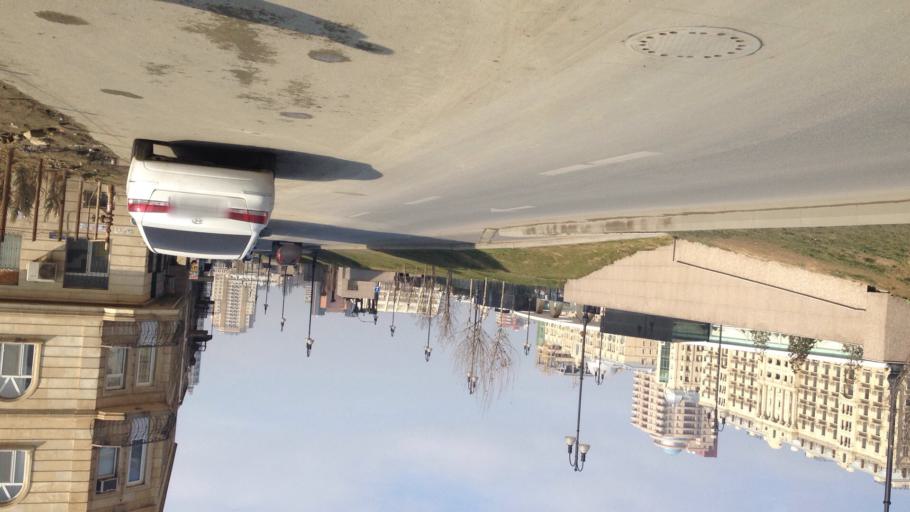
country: AZ
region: Baki
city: Badamdar
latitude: 40.3756
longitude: 49.8360
